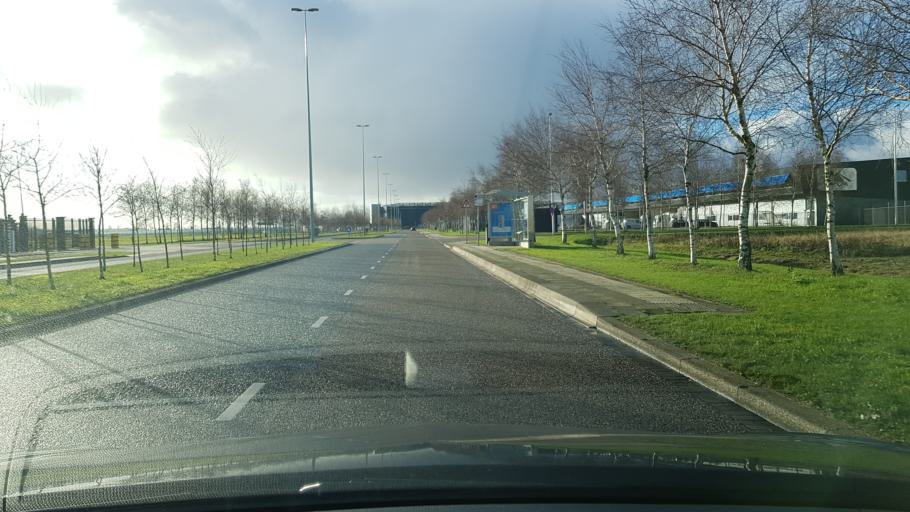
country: NL
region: North Holland
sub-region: Gemeente Aalsmeer
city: Aalsmeer
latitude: 52.2869
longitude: 4.7511
